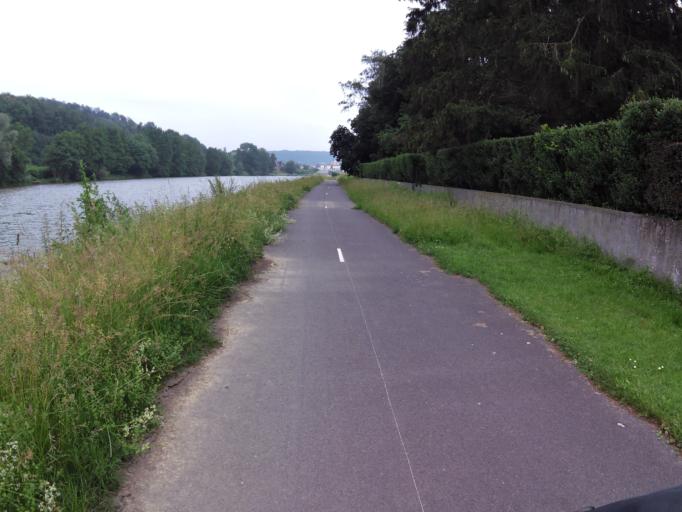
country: FR
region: Champagne-Ardenne
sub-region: Departement des Ardennes
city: Vireux-Wallerand
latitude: 50.0903
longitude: 4.7306
